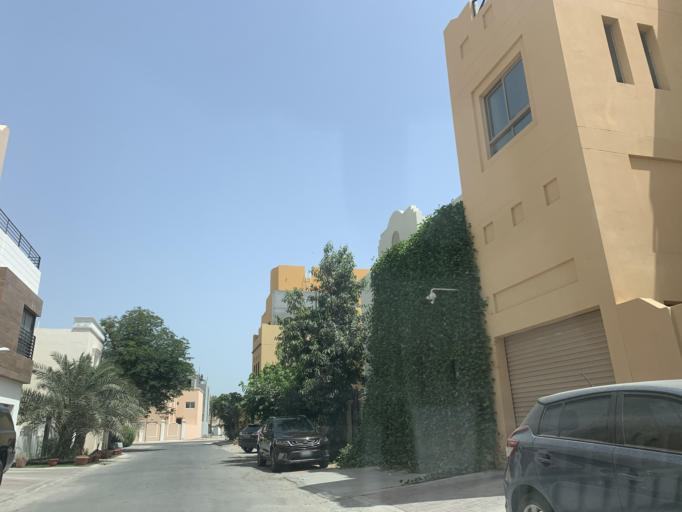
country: BH
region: Northern
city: Sitrah
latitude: 26.1575
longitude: 50.5828
